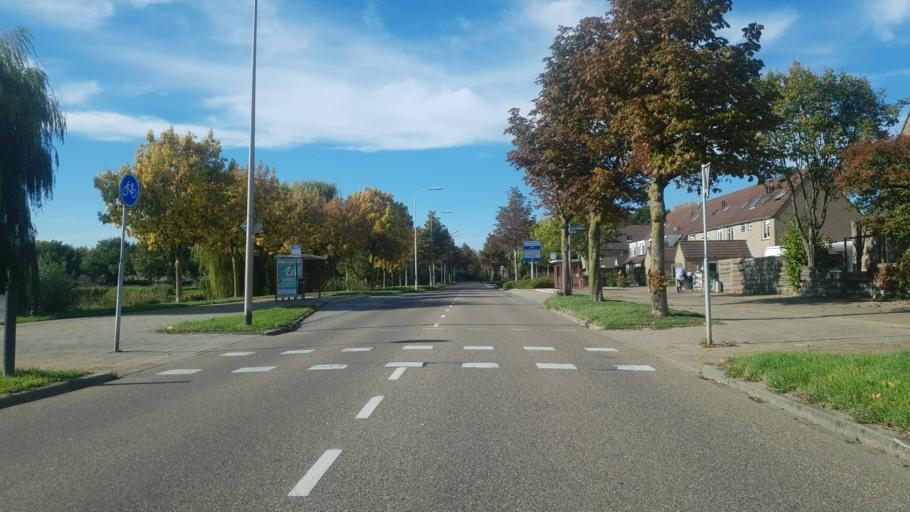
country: NL
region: Gelderland
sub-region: Gemeente Nijmegen
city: Lindenholt
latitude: 51.8277
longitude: 5.7813
